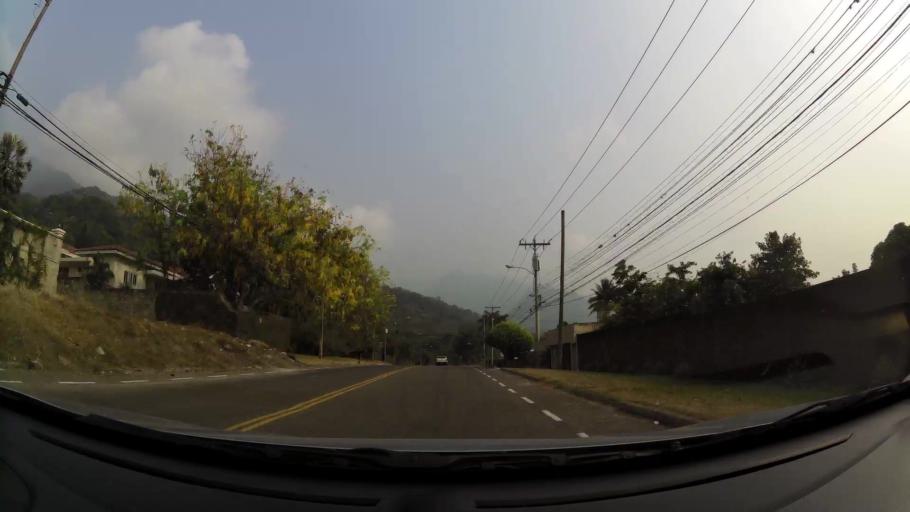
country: HN
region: Cortes
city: El Zapotal del Norte
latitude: 15.5109
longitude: -88.0491
